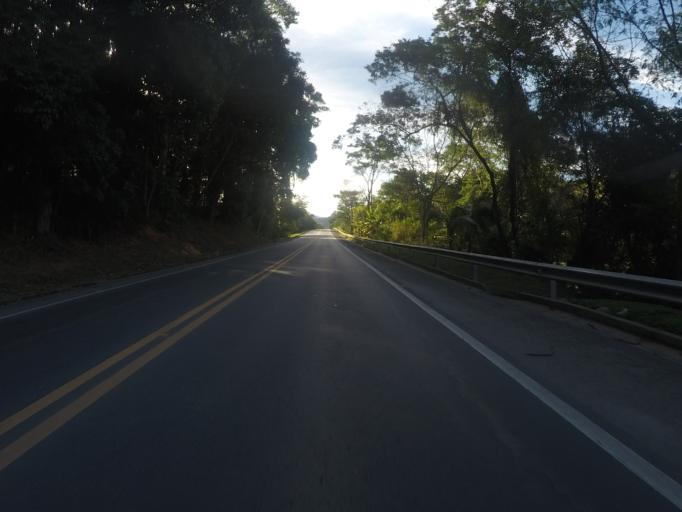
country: BR
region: Espirito Santo
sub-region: Fundao
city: Fundao
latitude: -19.8928
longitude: -40.4123
